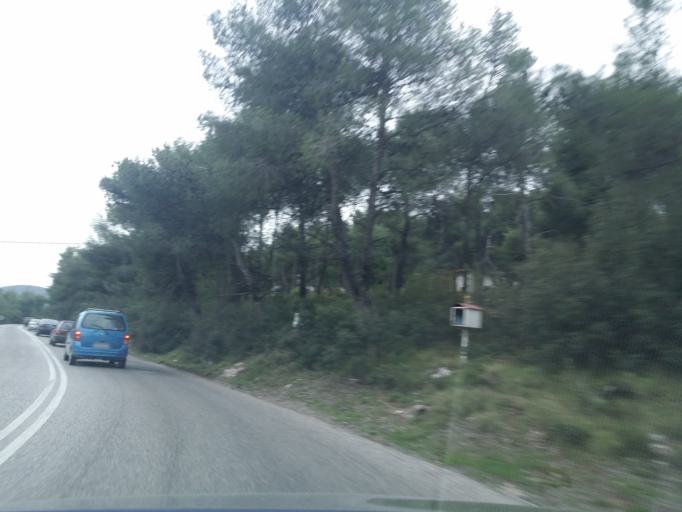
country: GR
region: Attica
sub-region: Nomarchia Dytikis Attikis
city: Vilia
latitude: 38.1273
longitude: 23.4107
